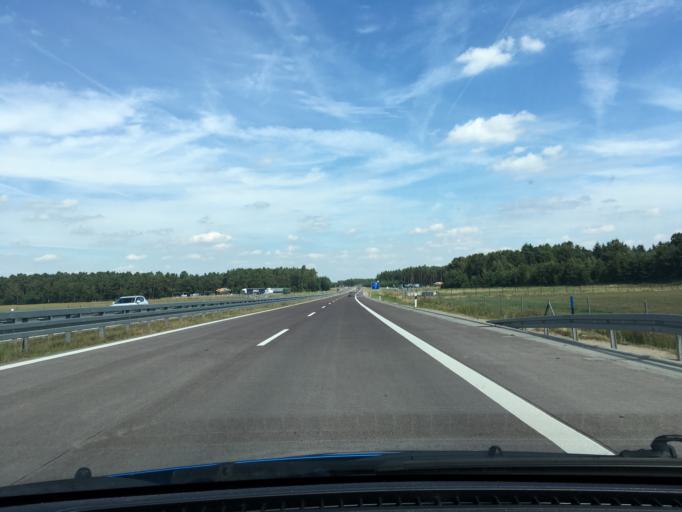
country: DE
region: Mecklenburg-Vorpommern
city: Gross Laasch
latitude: 53.3788
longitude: 11.5224
